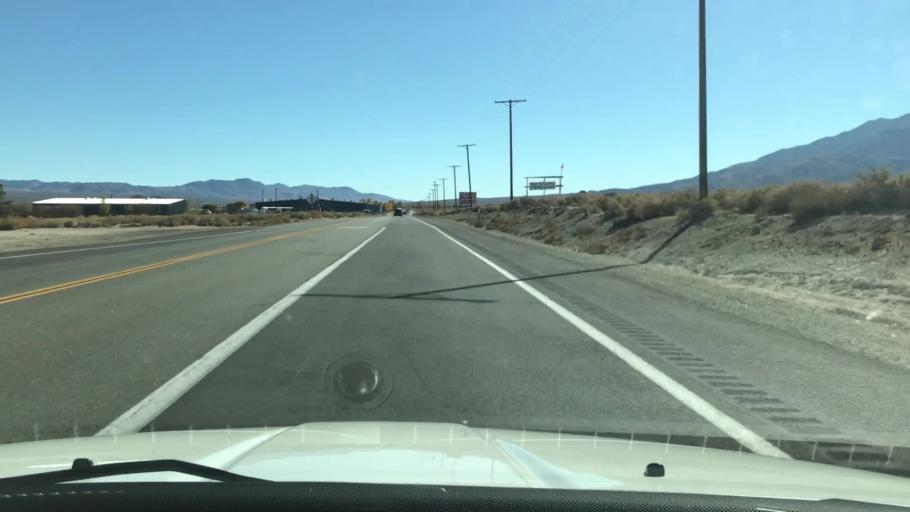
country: US
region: California
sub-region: Inyo County
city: Lone Pine
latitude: 36.3106
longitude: -118.0254
